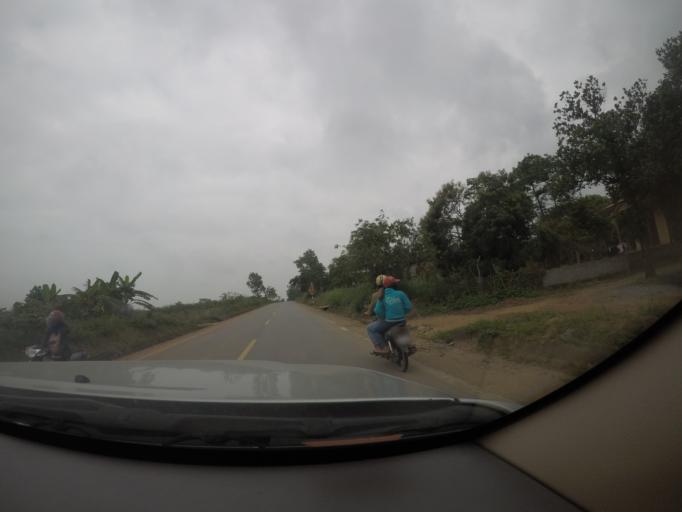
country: VN
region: Quang Binh
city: Hoan Lao
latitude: 17.5333
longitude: 106.4734
